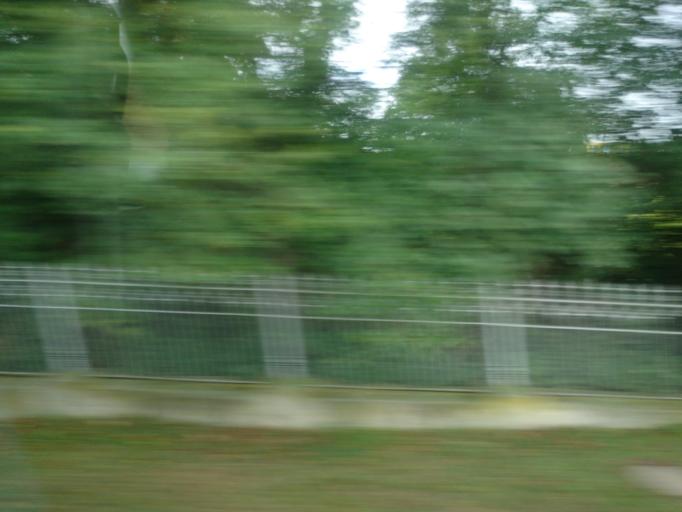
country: DE
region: Saxony-Anhalt
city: Grobers
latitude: 51.4282
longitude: 12.1181
